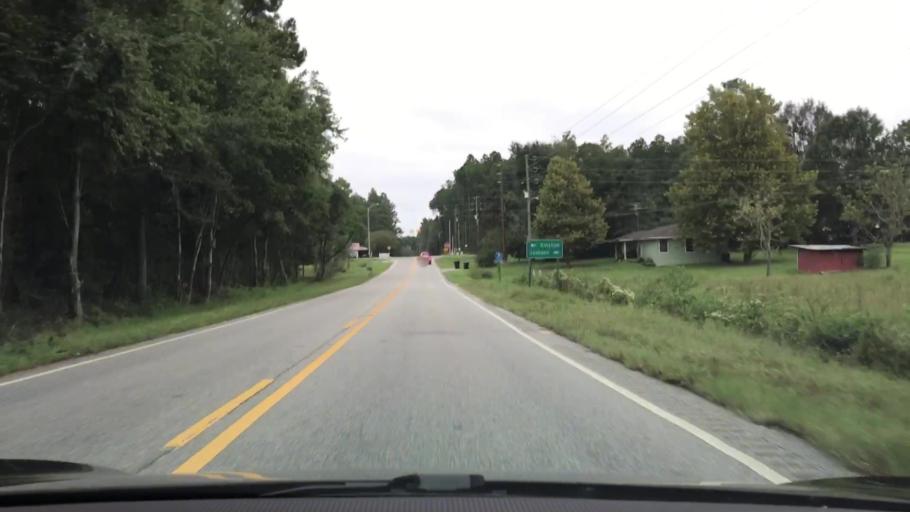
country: US
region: Alabama
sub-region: Geneva County
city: Samson
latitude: 31.1113
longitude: -86.1111
